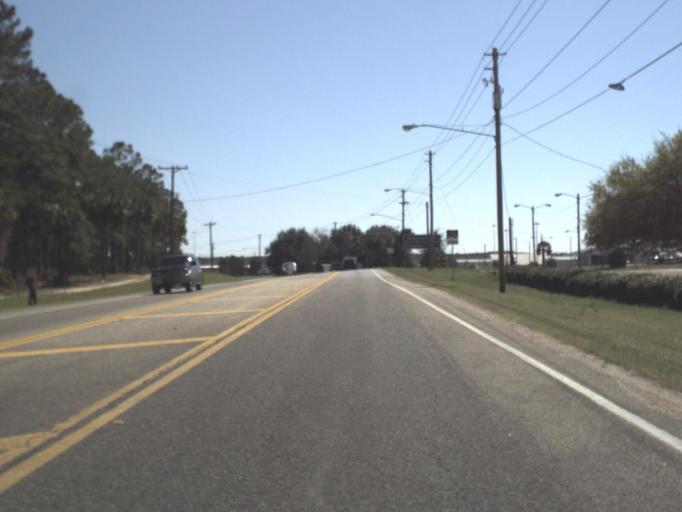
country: US
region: Florida
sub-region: Leon County
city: Tallahassee
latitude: 30.4028
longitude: -84.3531
